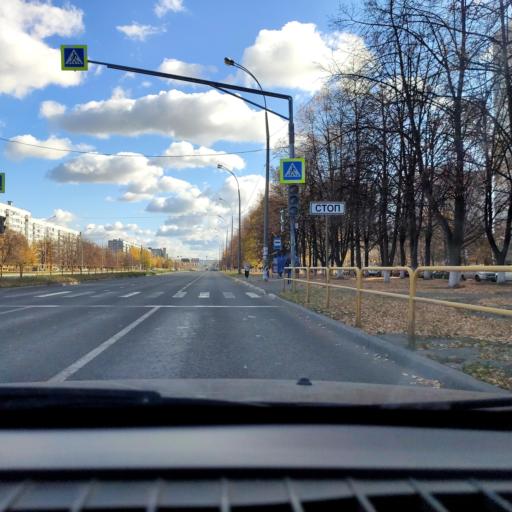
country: RU
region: Samara
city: Tol'yatti
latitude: 53.5267
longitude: 49.3051
